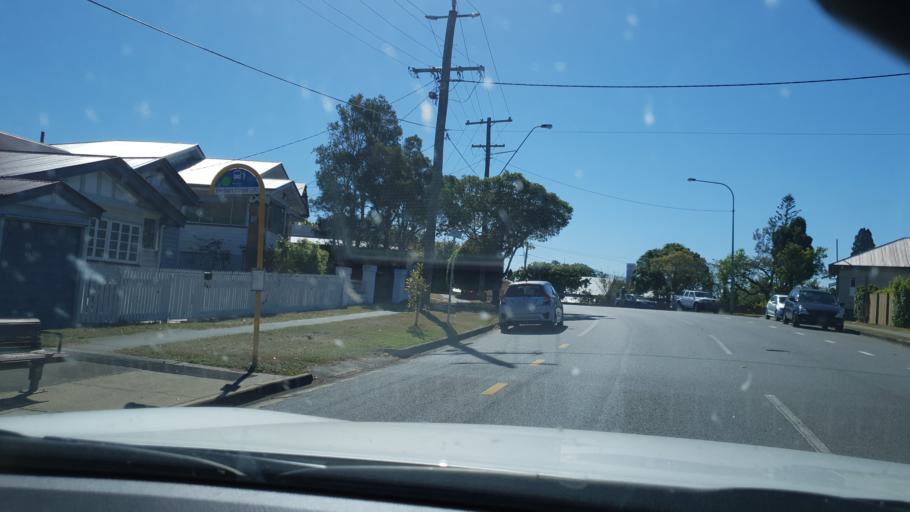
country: AU
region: Queensland
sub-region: Brisbane
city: Annerley
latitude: -27.5052
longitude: 153.0323
